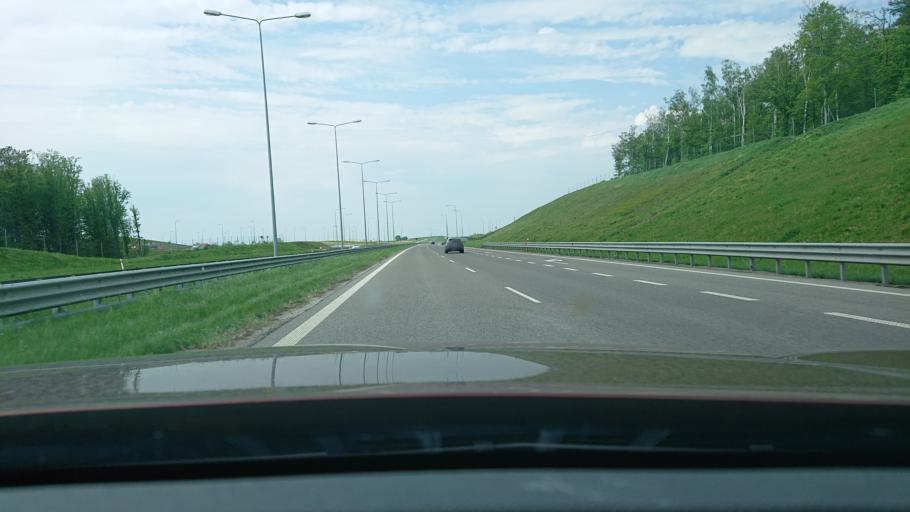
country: PL
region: Subcarpathian Voivodeship
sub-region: Powiat jaroslawski
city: Wierzbna
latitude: 50.0006
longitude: 22.6023
